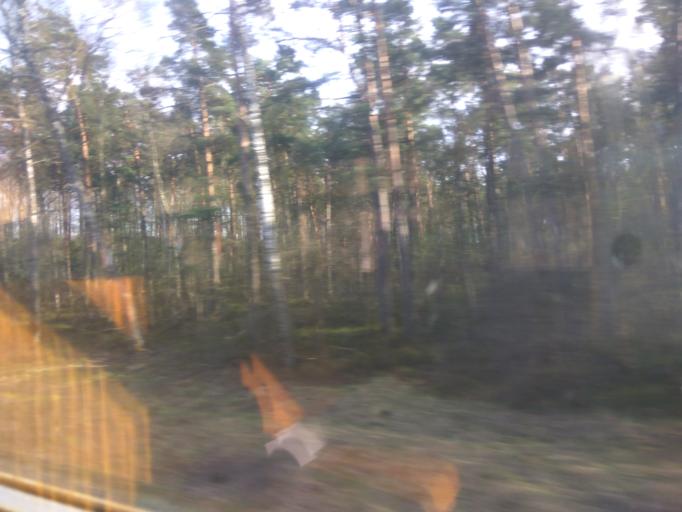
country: LV
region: Babite
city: Pinki
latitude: 56.9652
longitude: 23.9146
